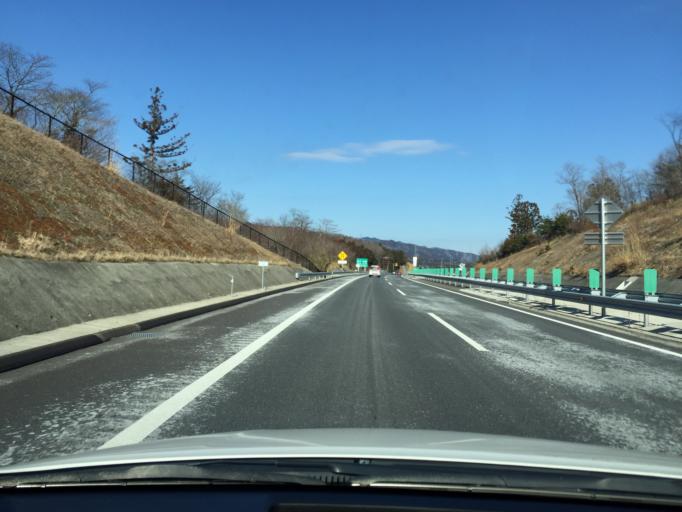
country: JP
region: Fukushima
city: Namie
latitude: 37.4931
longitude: 140.9458
